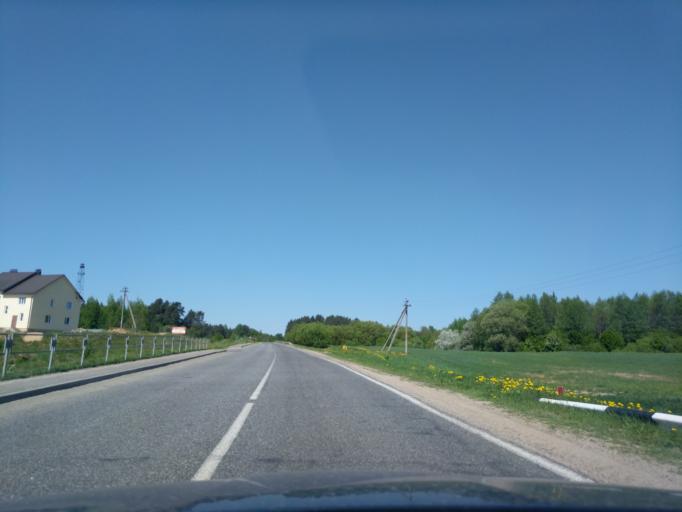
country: BY
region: Minsk
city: Myadzyel
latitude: 54.8929
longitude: 26.9108
